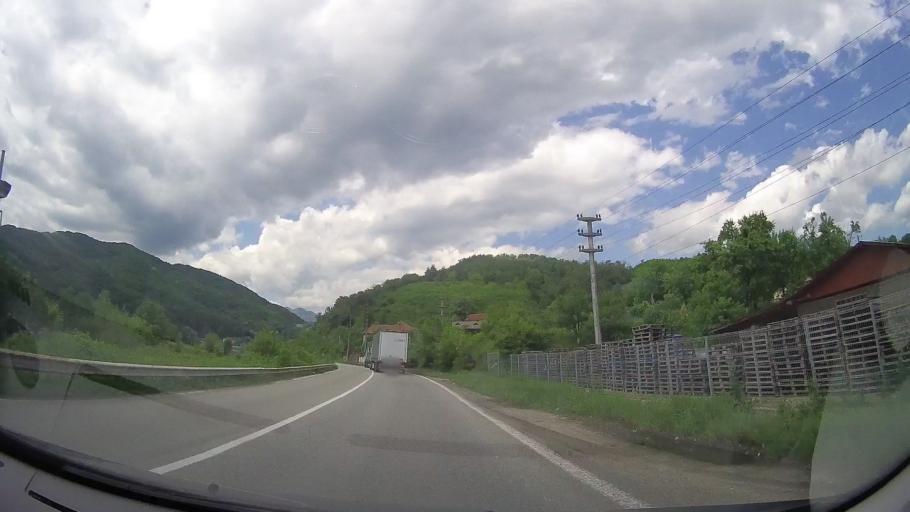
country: RO
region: Valcea
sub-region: Oras Calimanesti
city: Jiblea Veche
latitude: 45.2458
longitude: 24.3473
